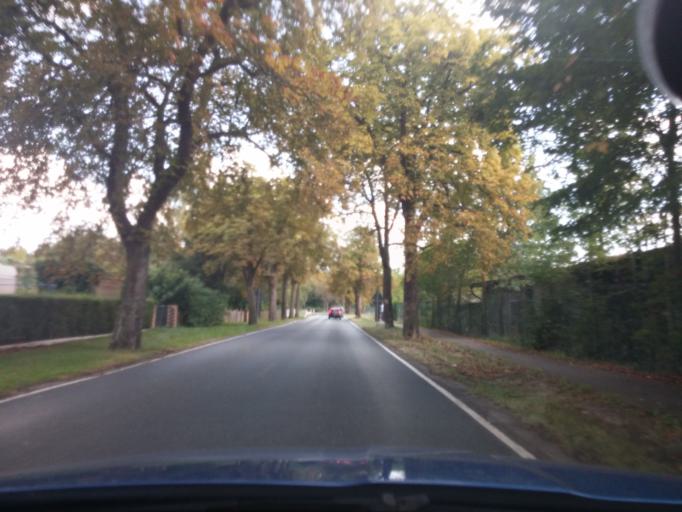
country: DE
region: Brandenburg
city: Halbe
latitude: 52.1068
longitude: 13.7055
